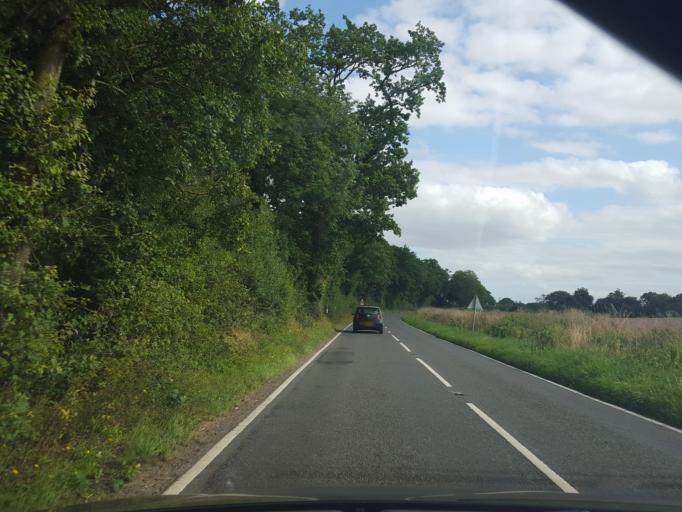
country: GB
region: England
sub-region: Essex
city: Mistley
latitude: 51.9332
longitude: 1.1761
